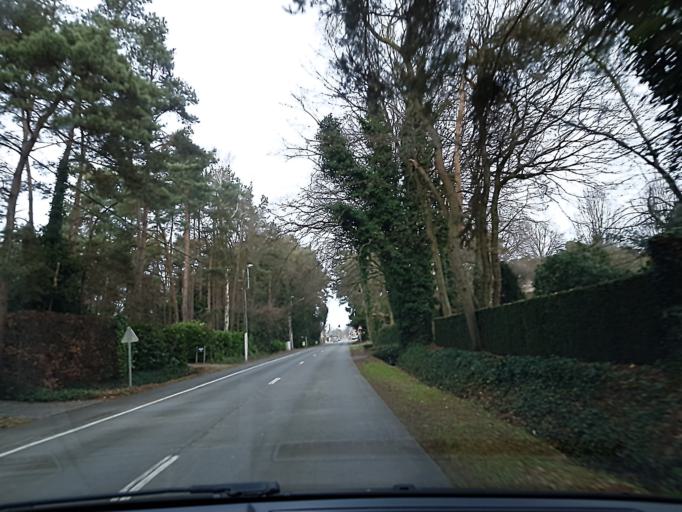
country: BE
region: Flanders
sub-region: Provincie Vlaams-Brabant
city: Keerbergen
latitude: 51.0220
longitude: 4.6025
